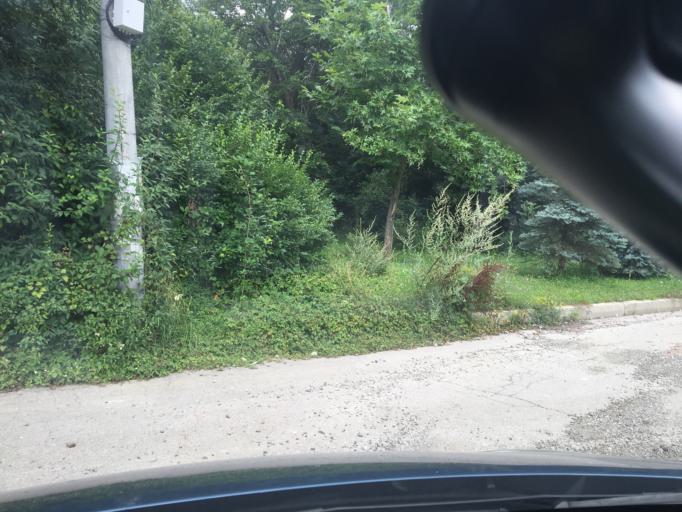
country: BG
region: Sofia-Capital
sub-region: Stolichna Obshtina
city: Sofia
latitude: 42.5835
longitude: 23.3610
